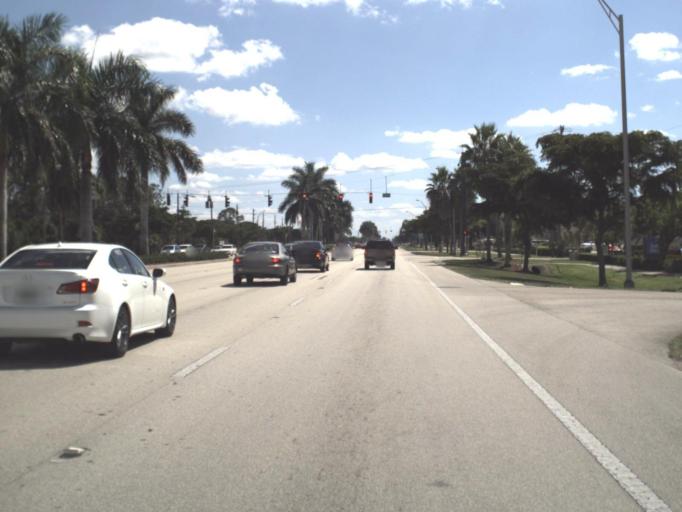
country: US
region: Florida
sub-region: Collier County
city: Lely
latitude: 26.1188
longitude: -81.7587
